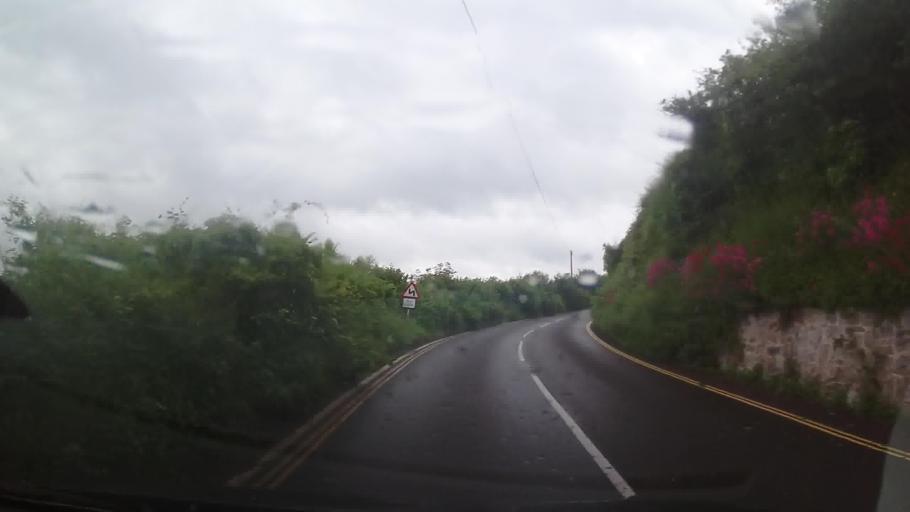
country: GB
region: England
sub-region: Devon
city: Dartmouth
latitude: 50.3610
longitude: -3.5736
